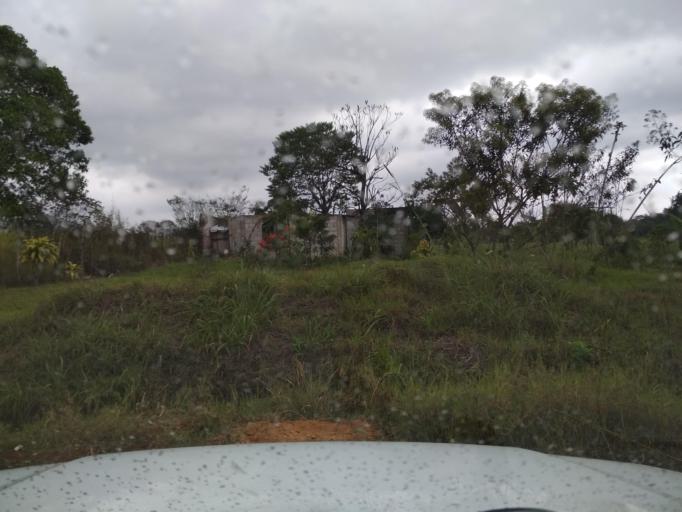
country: MX
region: Veracruz
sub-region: Cordoba
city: Veinte de Noviembre
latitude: 18.8731
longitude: -96.9535
